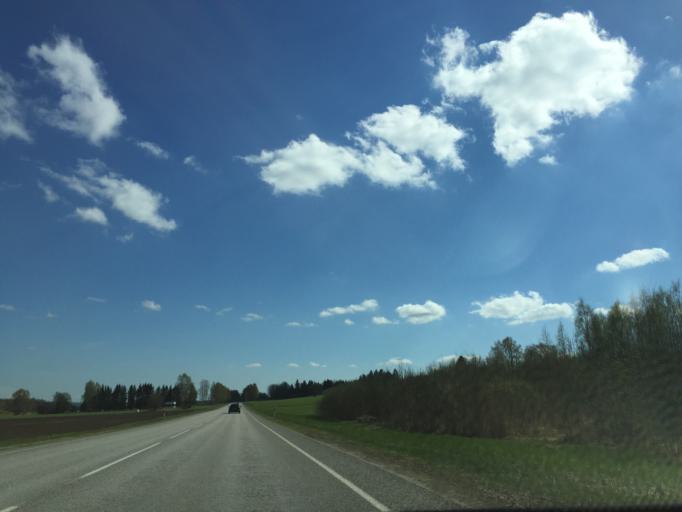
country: EE
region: Valgamaa
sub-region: Valga linn
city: Valga
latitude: 57.8972
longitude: 26.0520
